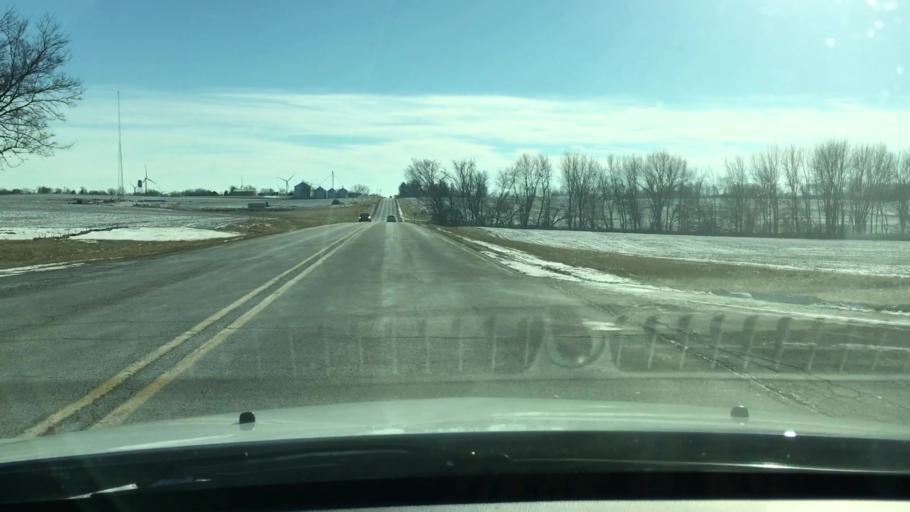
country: US
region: Illinois
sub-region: LaSalle County
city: Mendota
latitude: 41.7069
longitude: -89.0915
